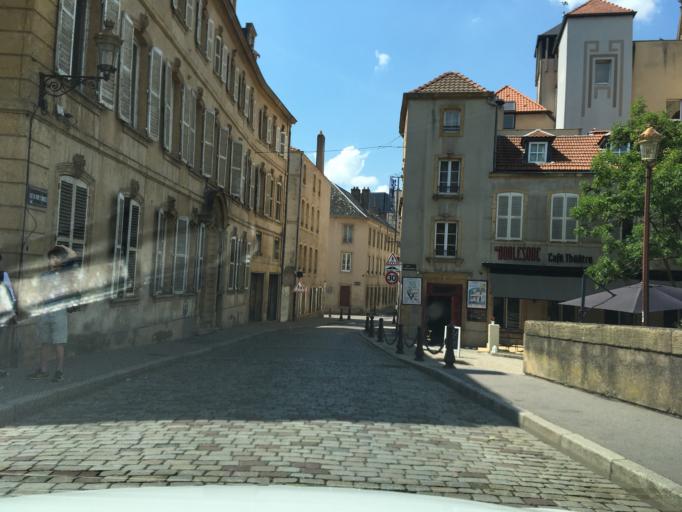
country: FR
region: Lorraine
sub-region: Departement de la Moselle
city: Metz
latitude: 49.1211
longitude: 6.1715
